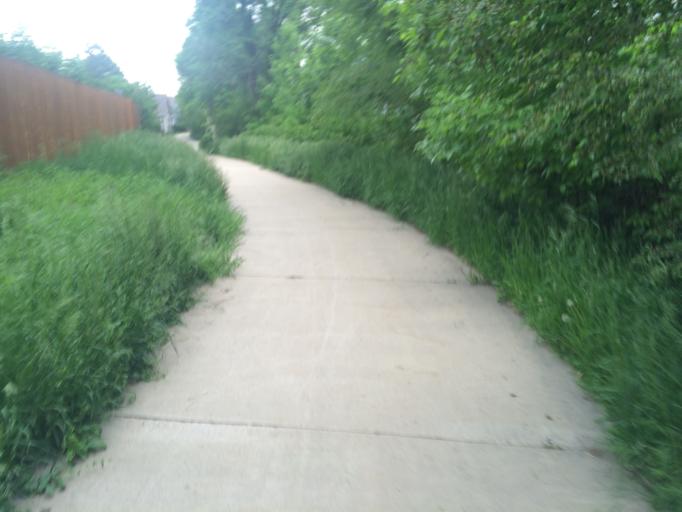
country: US
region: Colorado
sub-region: Boulder County
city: Boulder
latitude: 40.0294
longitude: -105.2413
